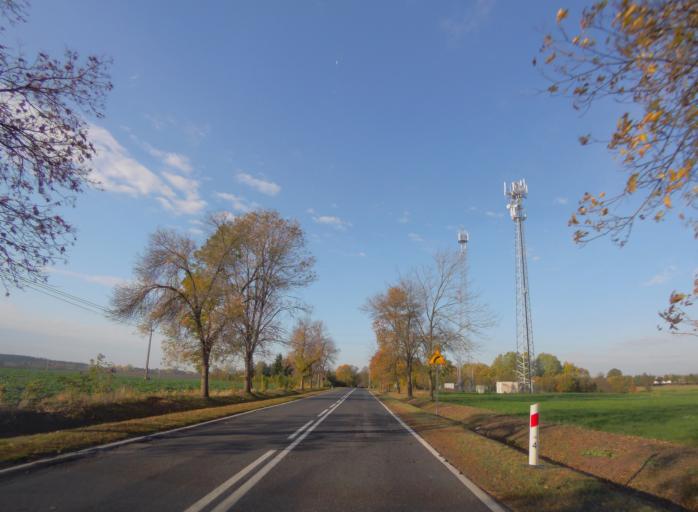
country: PL
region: Masovian Voivodeship
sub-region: Powiat siedlecki
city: Mordy
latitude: 52.2124
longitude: 22.5329
